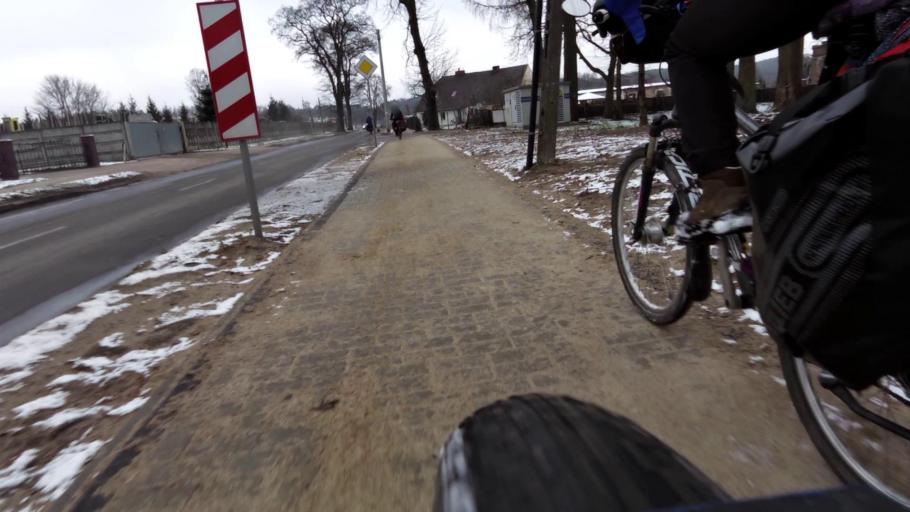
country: PL
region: West Pomeranian Voivodeship
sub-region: Powiat walecki
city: Miroslawiec
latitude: 53.3477
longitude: 16.0870
